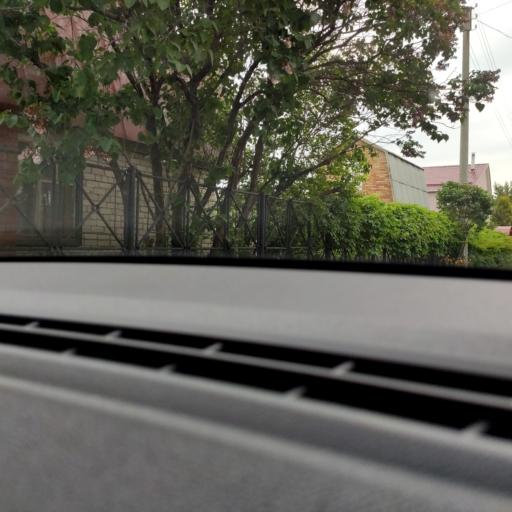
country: RU
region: Samara
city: Podstepki
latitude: 53.5049
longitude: 49.1609
